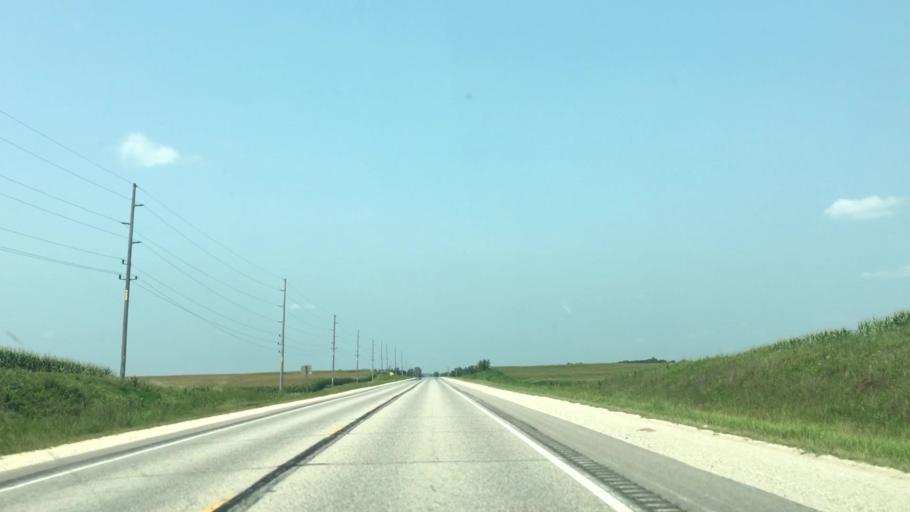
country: US
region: Iowa
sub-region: Fayette County
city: Fayette
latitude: 42.8851
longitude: -91.8105
